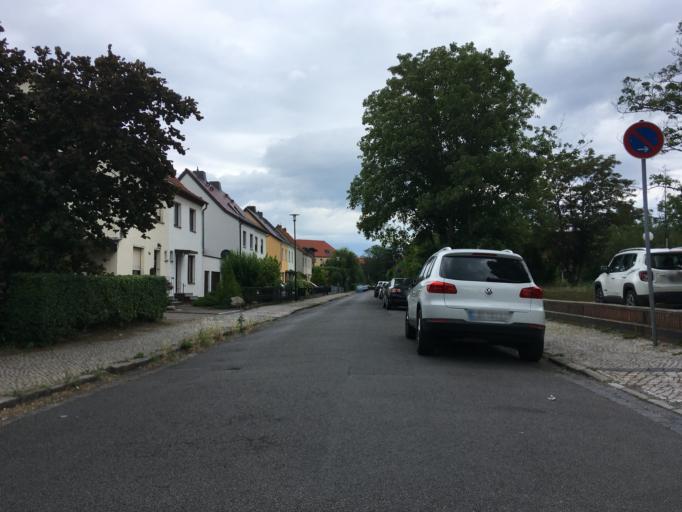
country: DE
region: Saxony-Anhalt
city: Dessau
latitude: 51.8369
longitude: 12.2246
